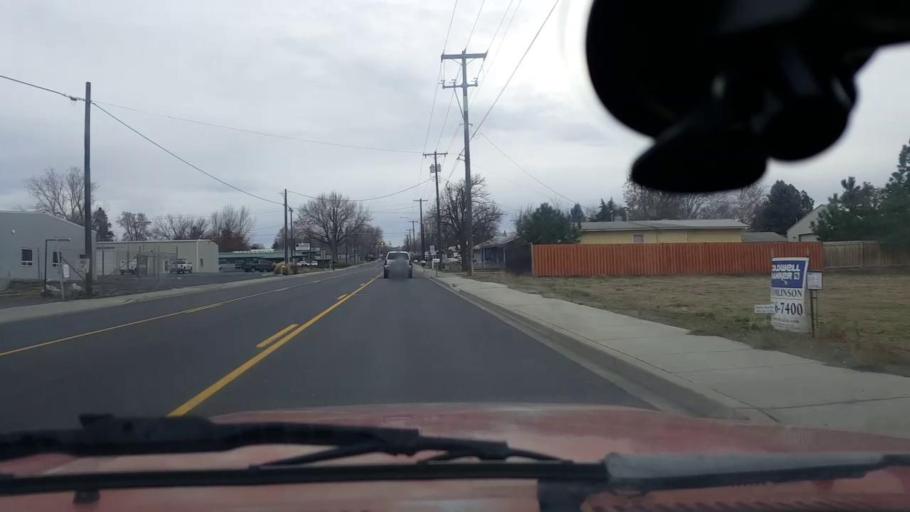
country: US
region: Washington
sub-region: Asotin County
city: West Clarkston-Highland
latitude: 46.4158
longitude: -117.0692
